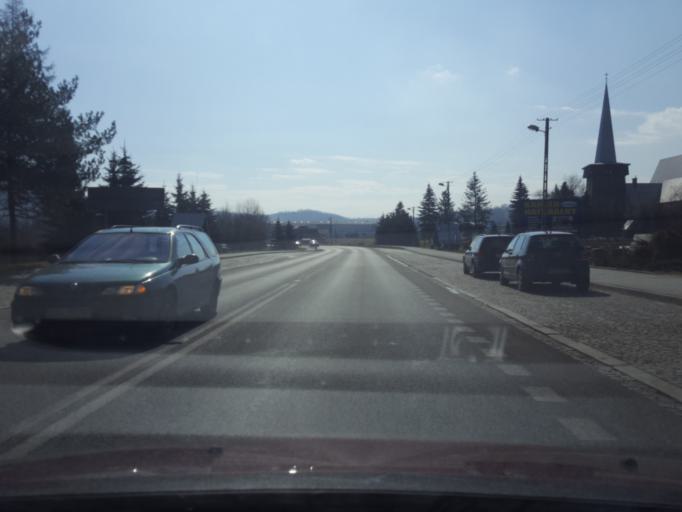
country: PL
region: Lesser Poland Voivodeship
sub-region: Powiat nowosadecki
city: Lososina Dolna
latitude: 49.7094
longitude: 20.6443
